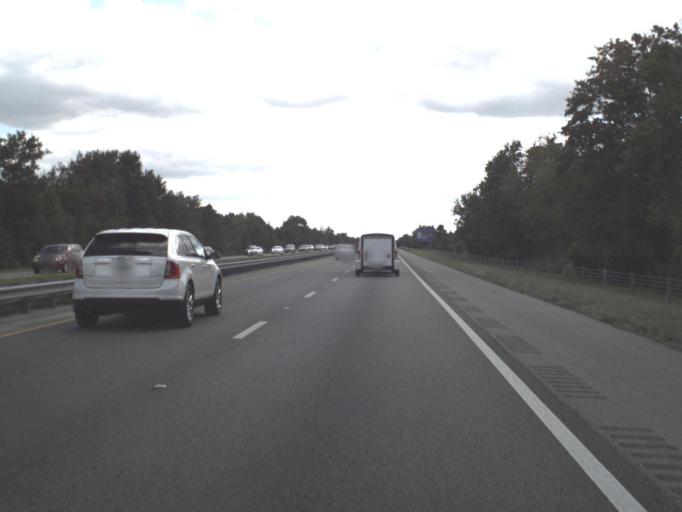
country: US
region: Florida
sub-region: Osceola County
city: Saint Cloud
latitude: 28.1460
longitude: -81.2953
